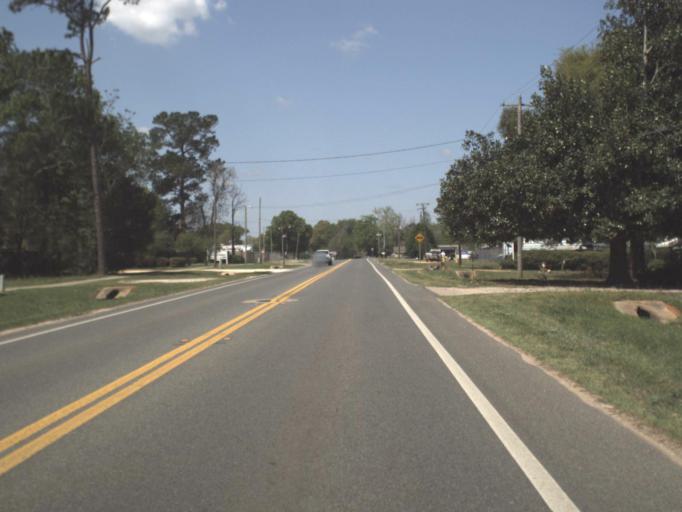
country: US
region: Florida
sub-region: Escambia County
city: Century
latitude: 30.9531
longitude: -87.1564
